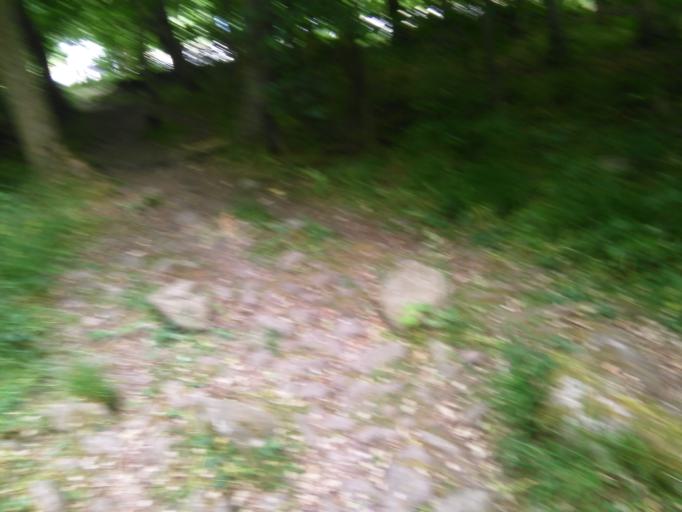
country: DK
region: Capital Region
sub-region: Bornholm Kommune
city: Akirkeby
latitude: 55.2376
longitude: 14.8713
